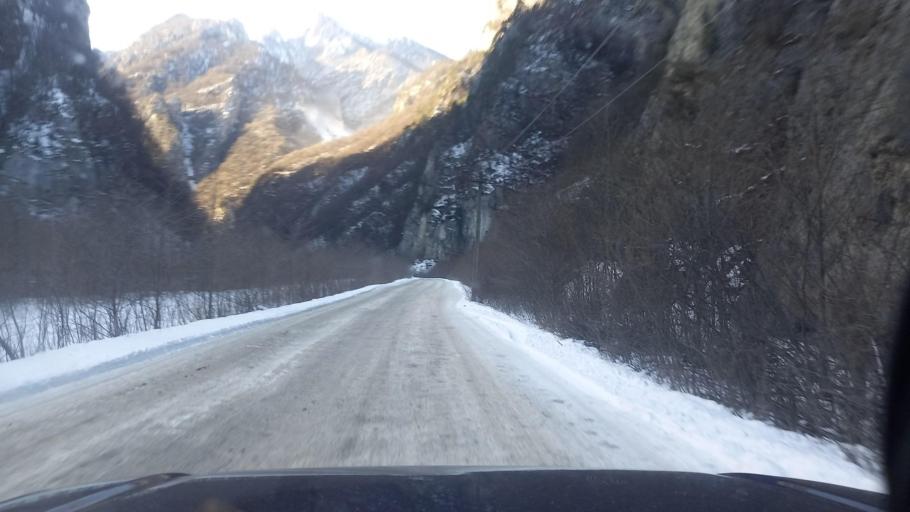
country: RU
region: North Ossetia
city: Gizel'
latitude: 42.8992
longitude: 44.5272
